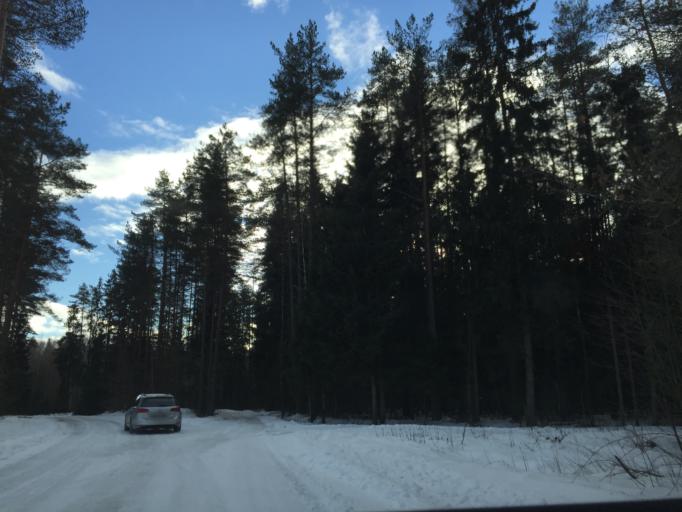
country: LV
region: Lielvarde
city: Lielvarde
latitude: 56.5634
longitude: 24.7983
